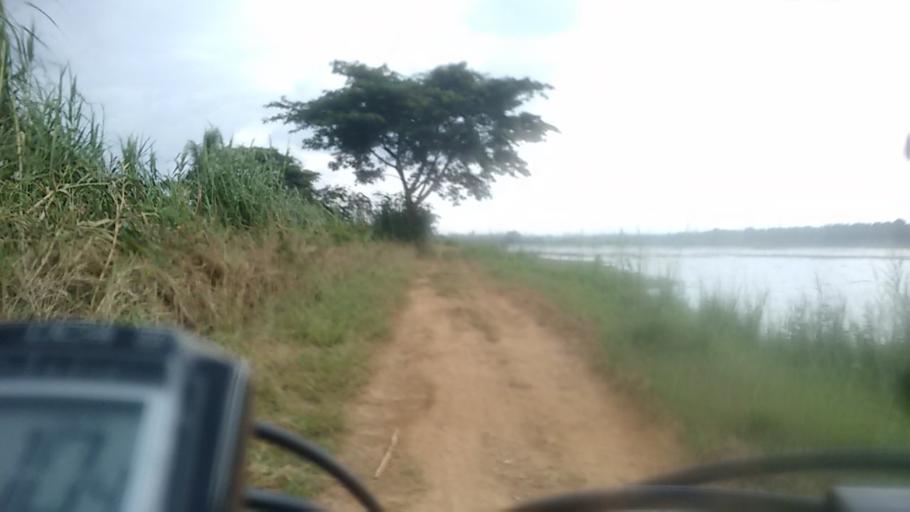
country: IN
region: Kerala
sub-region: Thrissur District
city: Trichur
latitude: 10.5310
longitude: 76.1594
